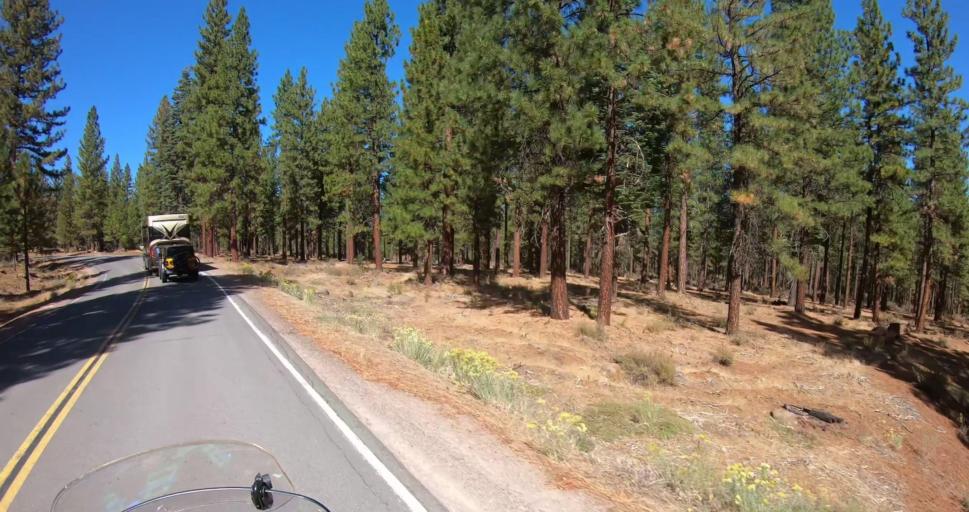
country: US
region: California
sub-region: Lassen County
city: Susanville
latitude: 40.4280
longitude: -120.7274
